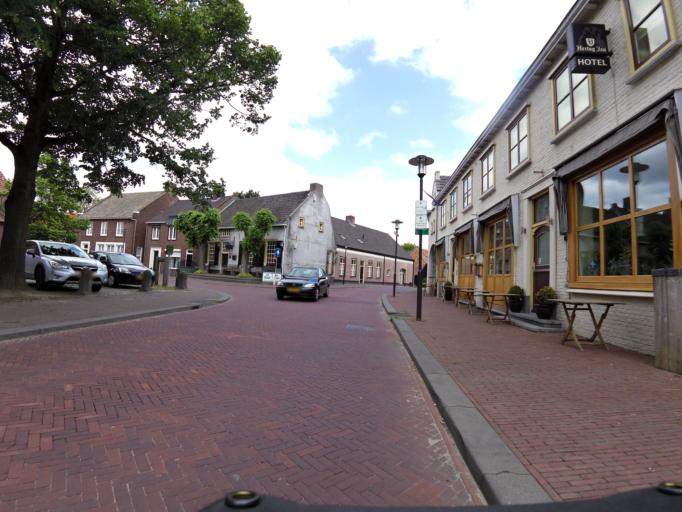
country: NL
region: North Brabant
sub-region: Gemeente Baarle-Nassau
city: Baarle-Nassau
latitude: 51.4844
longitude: 4.9555
